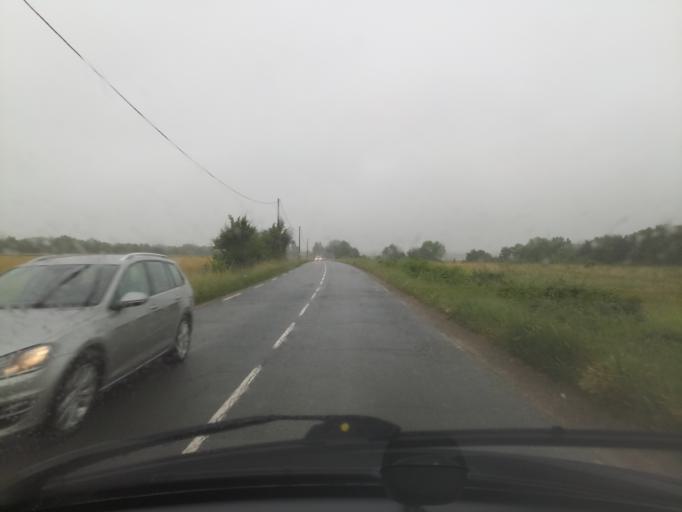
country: FR
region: Poitou-Charentes
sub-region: Departement de la Charente-Maritime
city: Saint-Jean-de-Liversay
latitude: 46.2382
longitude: -0.8814
